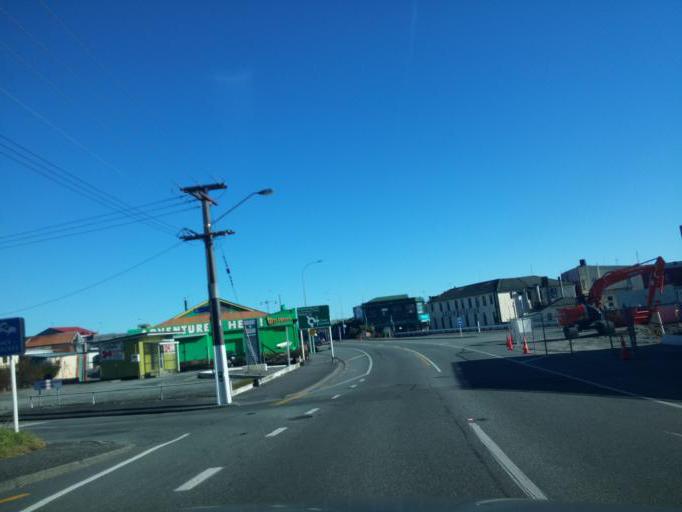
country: NZ
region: West Coast
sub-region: Grey District
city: Greymouth
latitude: -42.4496
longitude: 171.2129
